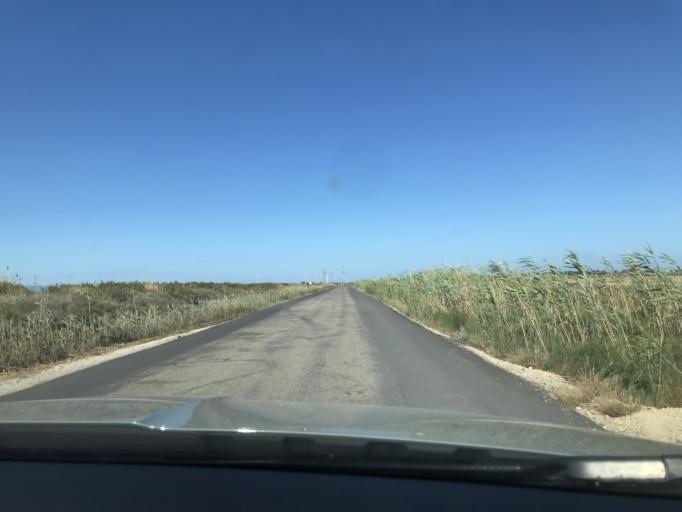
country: ES
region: Catalonia
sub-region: Provincia de Tarragona
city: Deltebre
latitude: 40.6463
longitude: 0.7571
